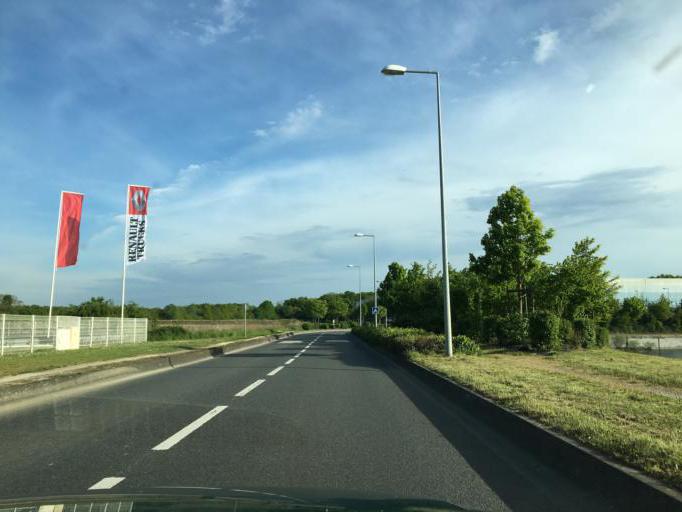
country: FR
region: Centre
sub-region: Departement du Loiret
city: Ormes
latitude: 47.9440
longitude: 1.8451
